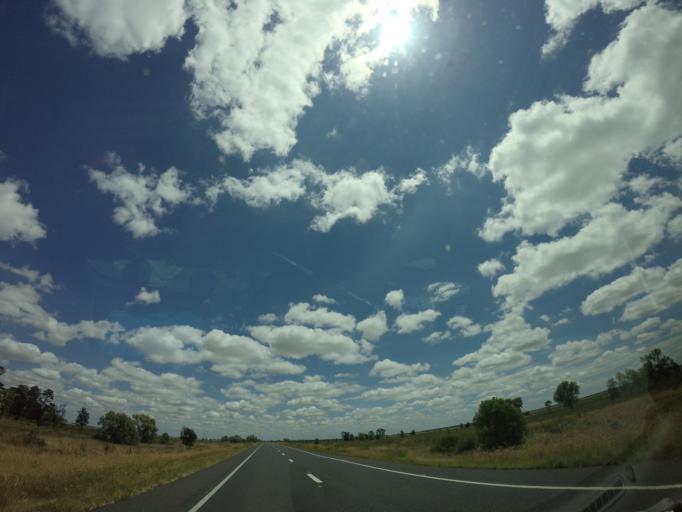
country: AU
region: New South Wales
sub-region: Moree Plains
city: Moree
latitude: -29.0614
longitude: 150.0450
